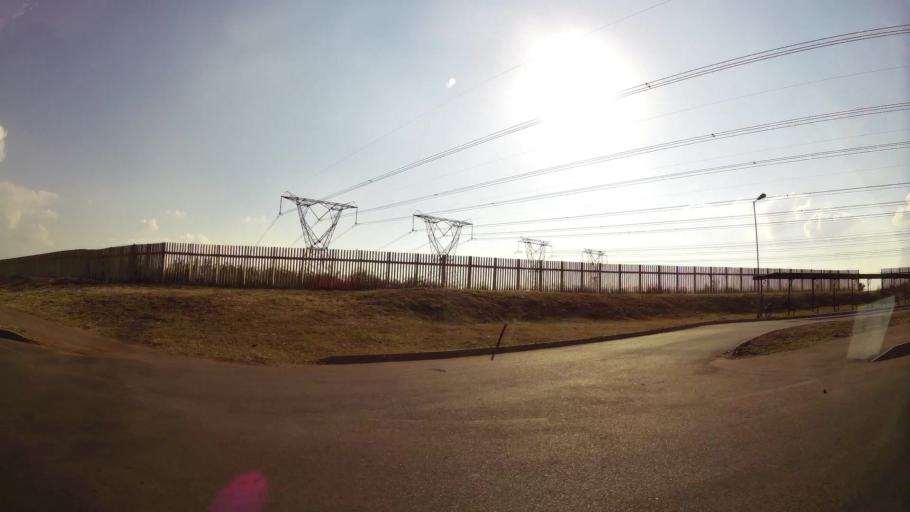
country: ZA
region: Gauteng
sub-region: City of Tshwane Metropolitan Municipality
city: Centurion
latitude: -25.9178
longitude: 28.2104
